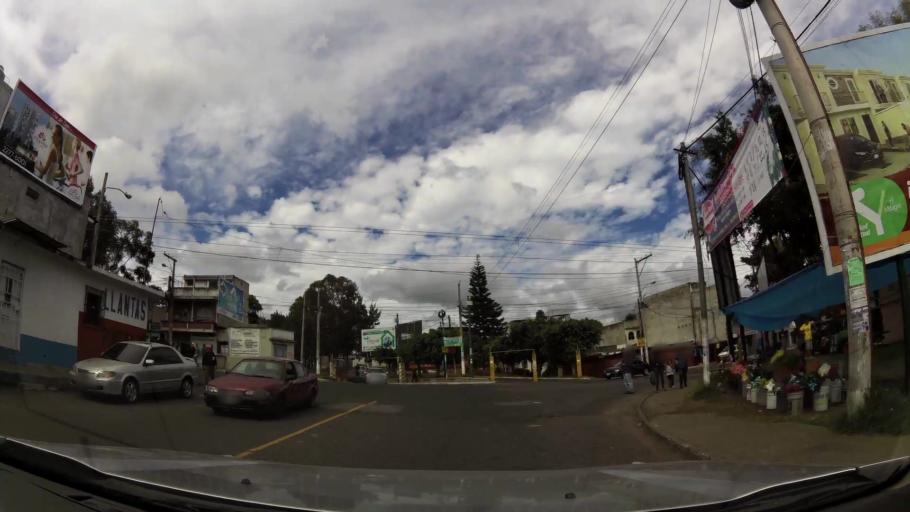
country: GT
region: Guatemala
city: Mixco
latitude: 14.6630
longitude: -90.5725
